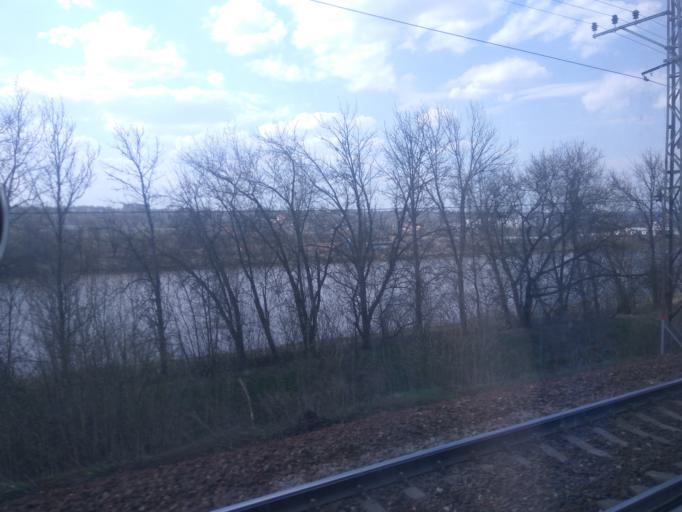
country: RU
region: Moskovskaya
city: Yakhroma
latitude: 56.2759
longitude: 37.5069
